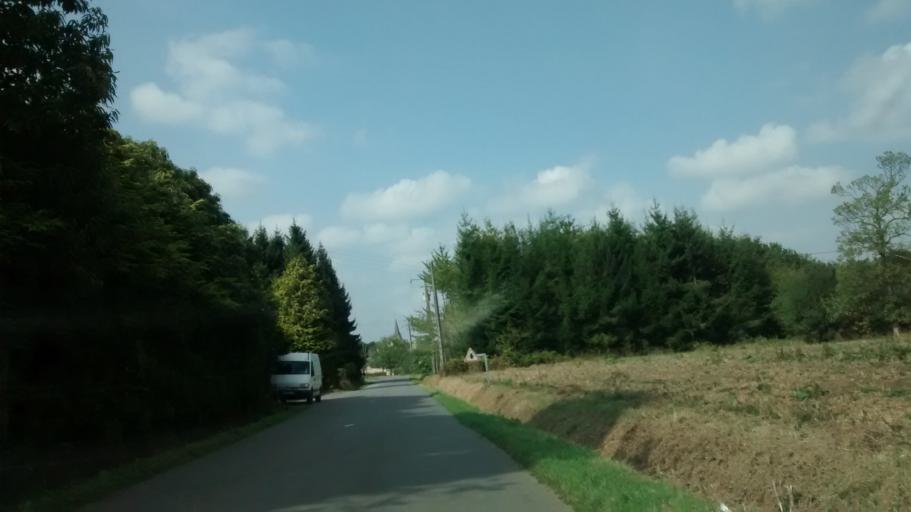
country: FR
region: Brittany
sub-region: Departement d'Ille-et-Vilaine
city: Livre-sur-Changeon
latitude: 48.2348
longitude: -1.2951
